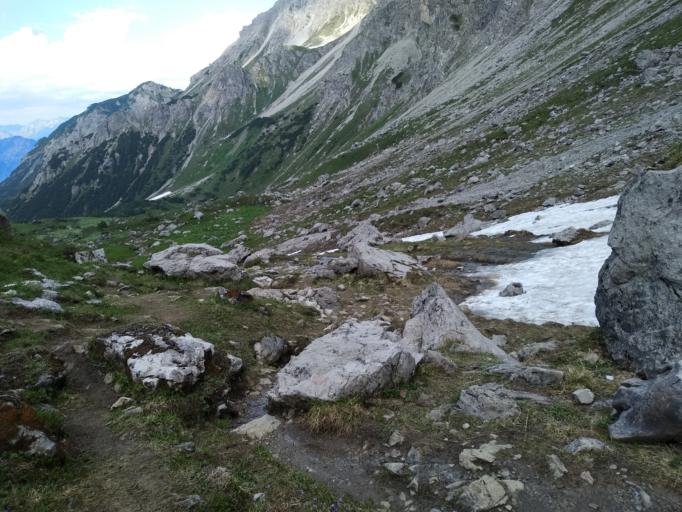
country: AT
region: Vorarlberg
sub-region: Politischer Bezirk Bregenz
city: Mittelberg
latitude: 47.3187
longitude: 10.2188
